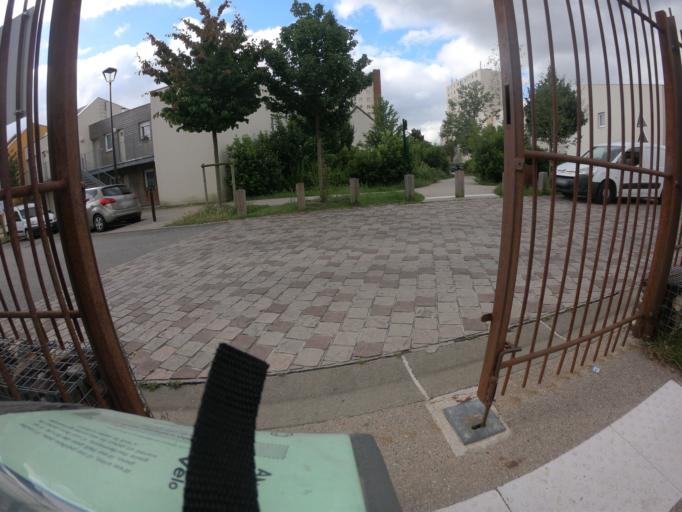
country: FR
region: Ile-de-France
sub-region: Departement des Hauts-de-Seine
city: Chatenay-Malabry
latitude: 48.7587
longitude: 2.2803
